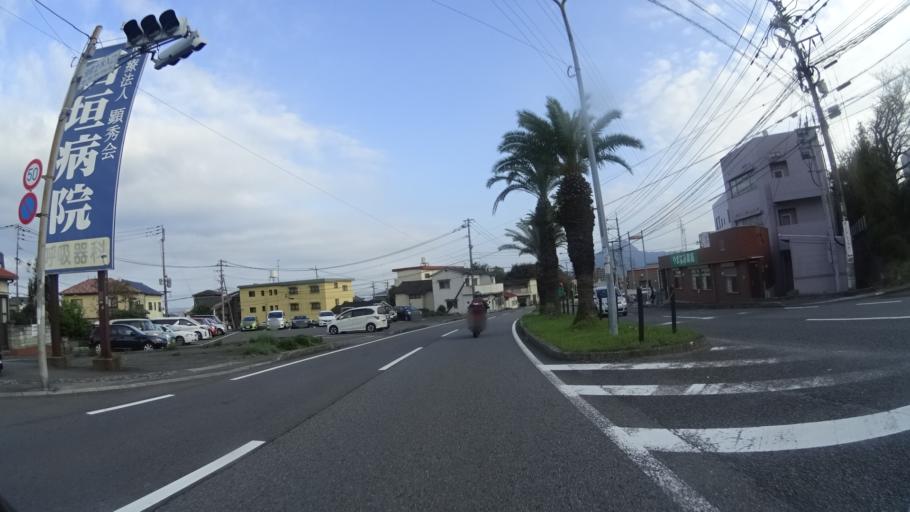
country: JP
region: Oita
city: Beppu
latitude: 33.3115
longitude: 131.4856
